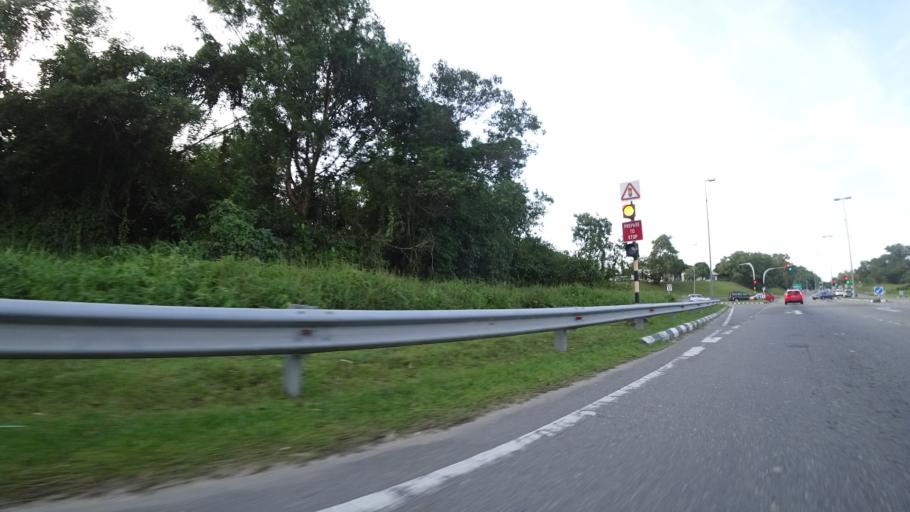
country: BN
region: Brunei and Muara
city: Bandar Seri Begawan
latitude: 4.8907
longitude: 114.9106
